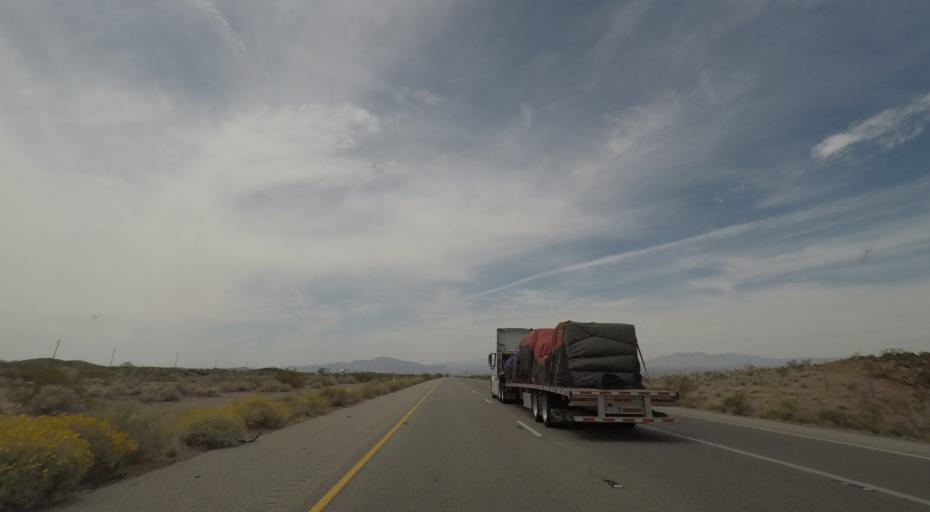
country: US
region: California
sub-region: San Bernardino County
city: Needles
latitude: 34.8286
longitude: -115.0607
